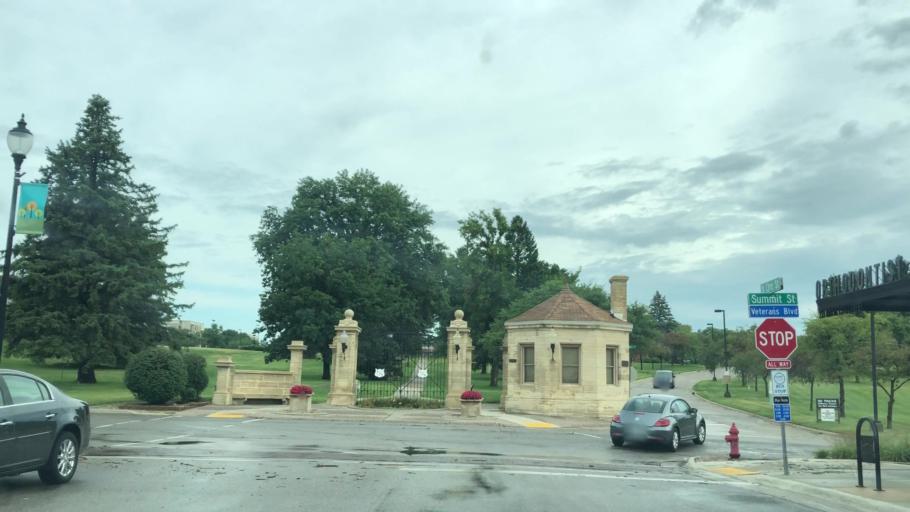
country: US
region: Iowa
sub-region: Marshall County
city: Marshalltown
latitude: 42.0525
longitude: -92.9347
